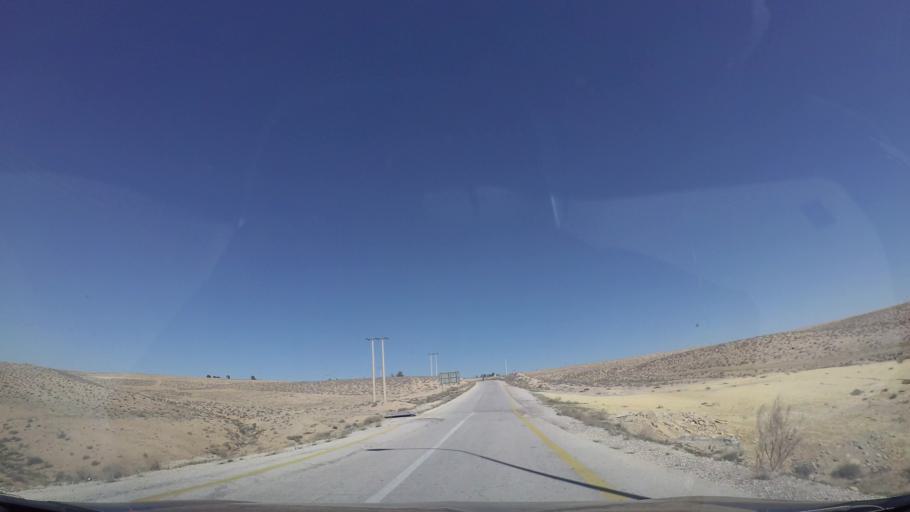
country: JO
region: Tafielah
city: Busayra
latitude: 30.5246
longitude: 35.6115
